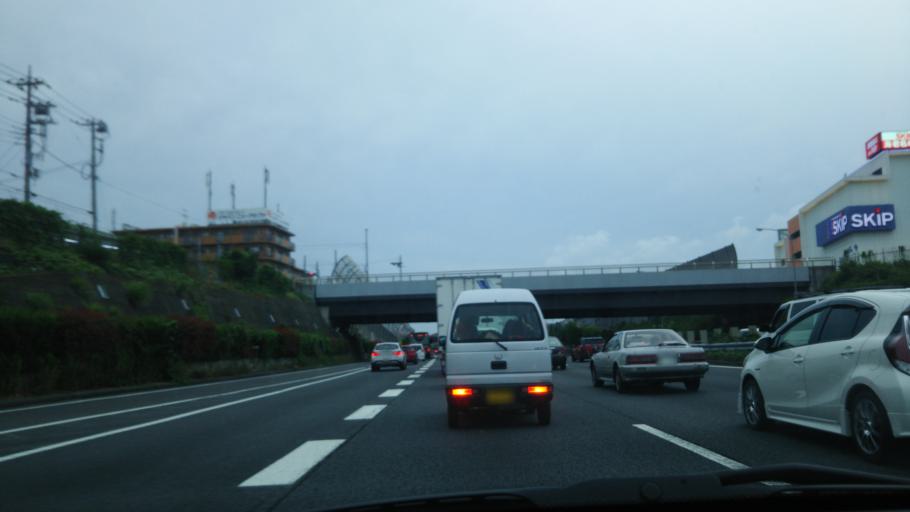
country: JP
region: Kanagawa
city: Minami-rinkan
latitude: 35.4482
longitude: 139.4193
